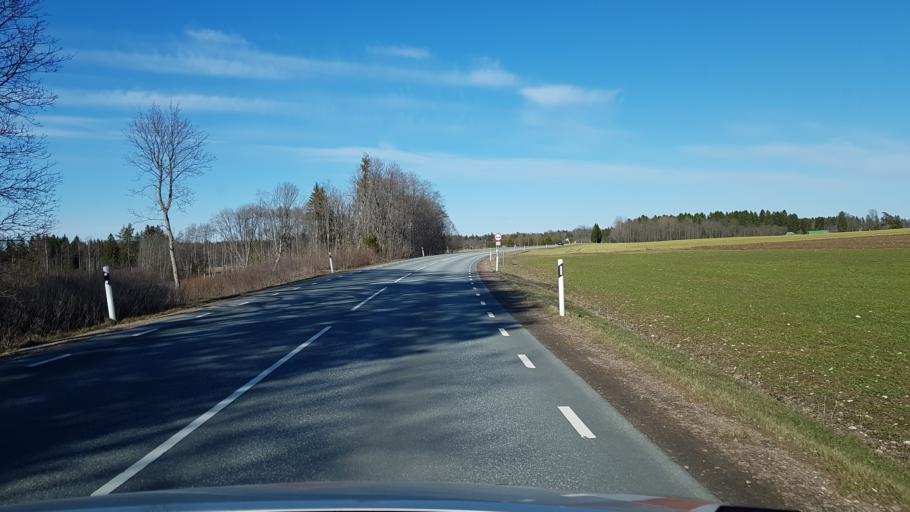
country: EE
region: Laeaene-Virumaa
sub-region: Tapa vald
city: Tapa
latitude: 59.3758
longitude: 26.0032
